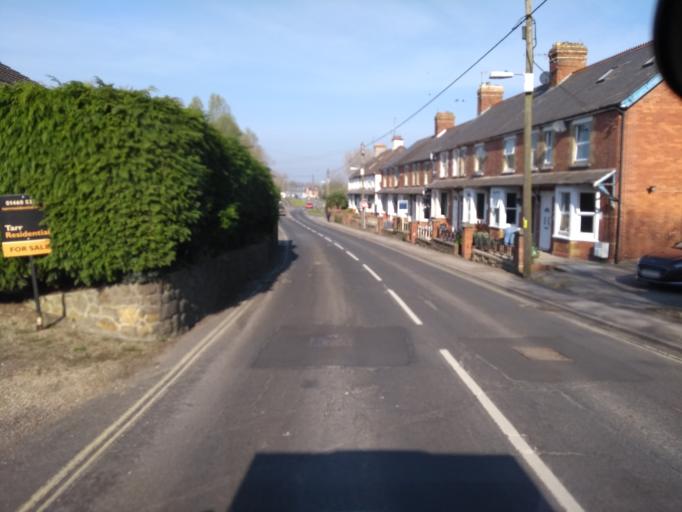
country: GB
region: England
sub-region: Somerset
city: Ilminster
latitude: 50.9294
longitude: -2.9207
